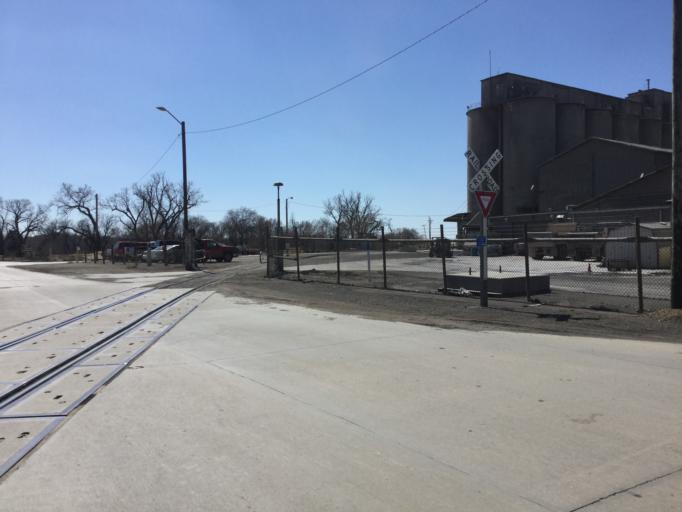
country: US
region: Kansas
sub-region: Allen County
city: Humboldt
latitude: 37.7971
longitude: -95.4290
